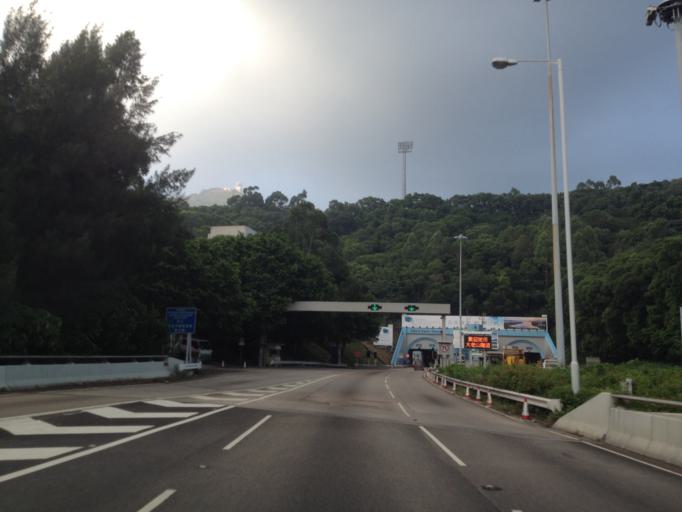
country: HK
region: Wong Tai Sin
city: Wong Tai Sin
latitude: 22.3404
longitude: 114.2035
